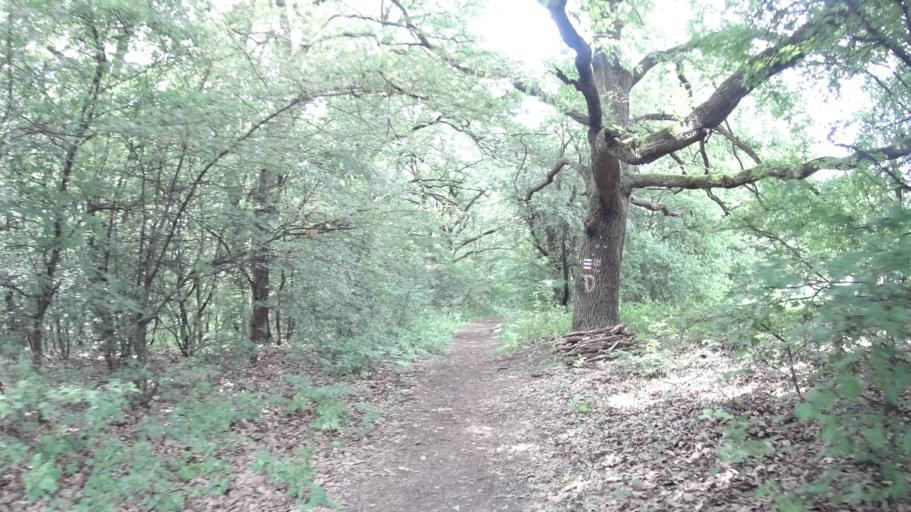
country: HU
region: Pest
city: Nagymaros
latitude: 47.8278
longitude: 18.9445
